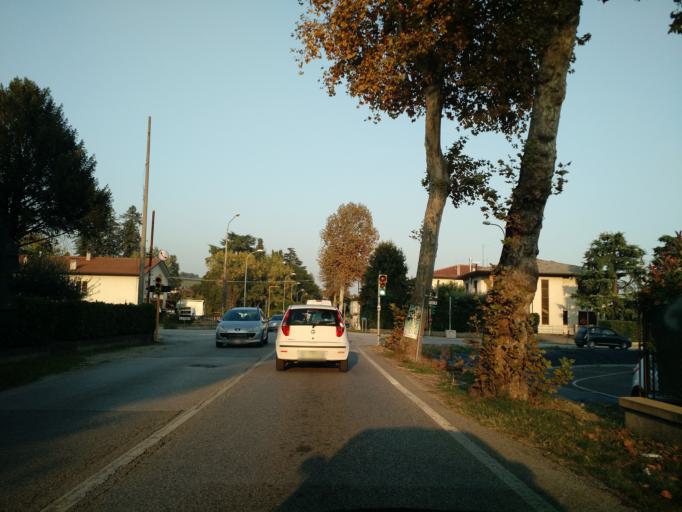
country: IT
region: Veneto
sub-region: Provincia di Vicenza
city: Breganze
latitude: 45.7065
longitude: 11.5470
